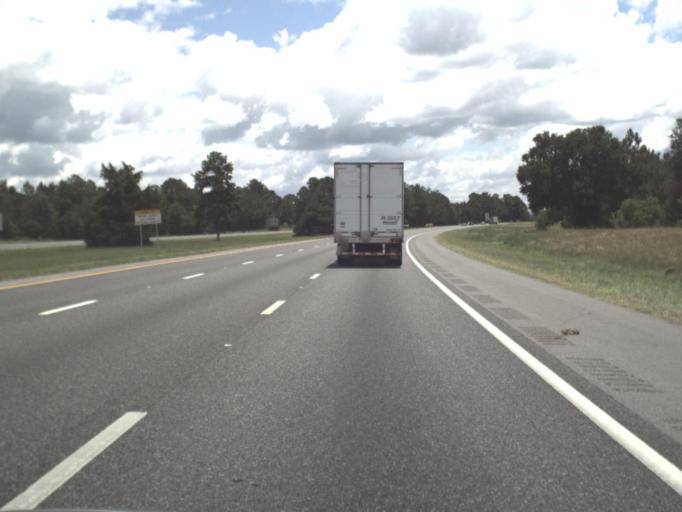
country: US
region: Florida
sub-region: Alachua County
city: High Springs
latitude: 29.9962
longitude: -82.5899
